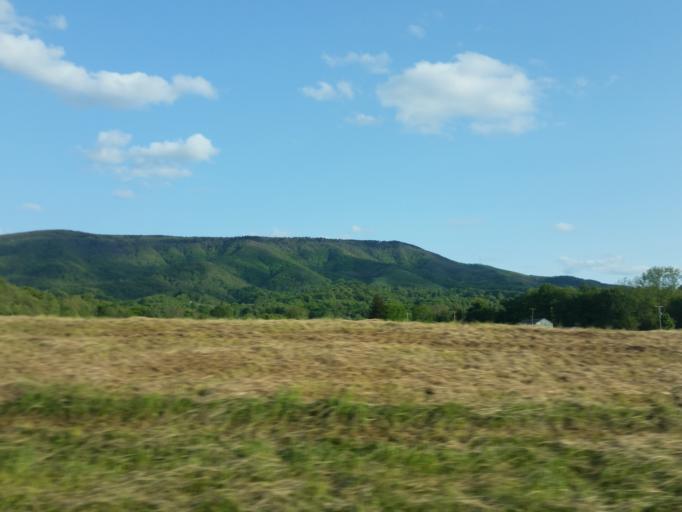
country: US
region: Virginia
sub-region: Russell County
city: Honaker
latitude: 36.9692
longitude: -81.9082
